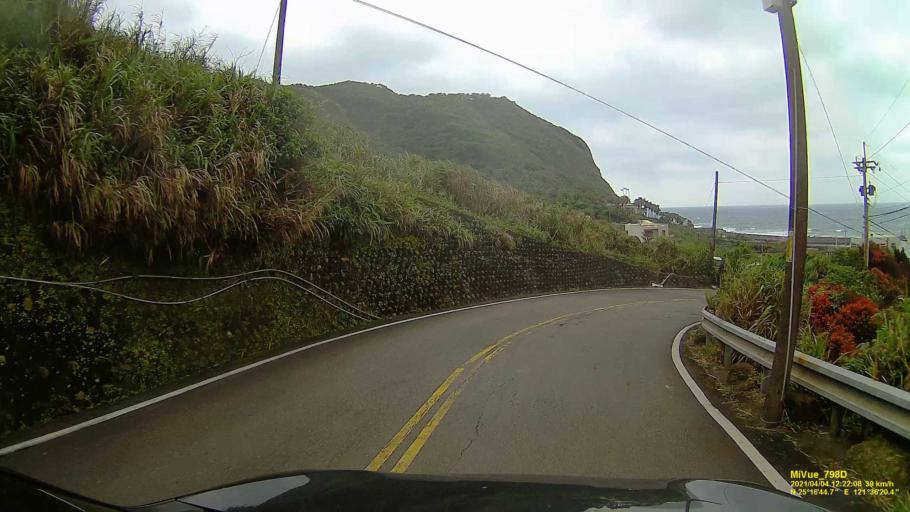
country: TW
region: Taiwan
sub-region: Keelung
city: Keelung
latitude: 25.2793
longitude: 121.6056
